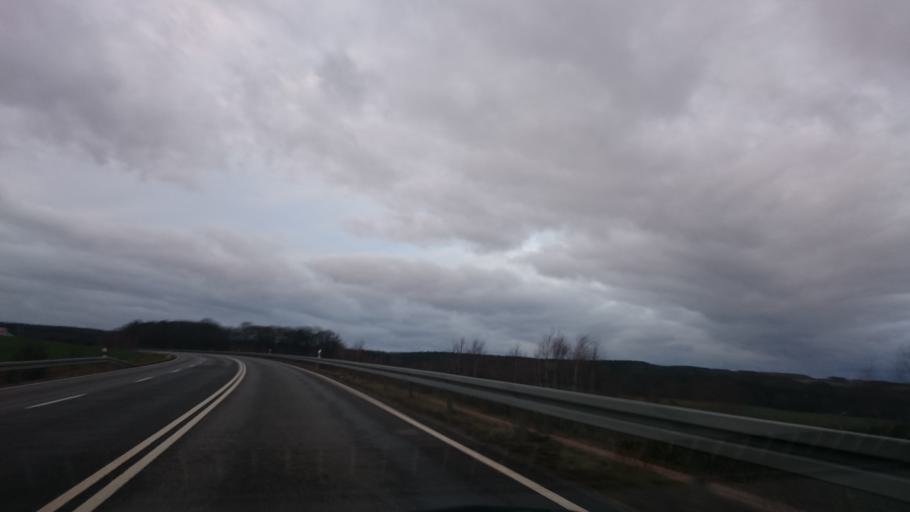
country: DE
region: Saxony
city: Hirschfeld
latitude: 50.6269
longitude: 12.4705
